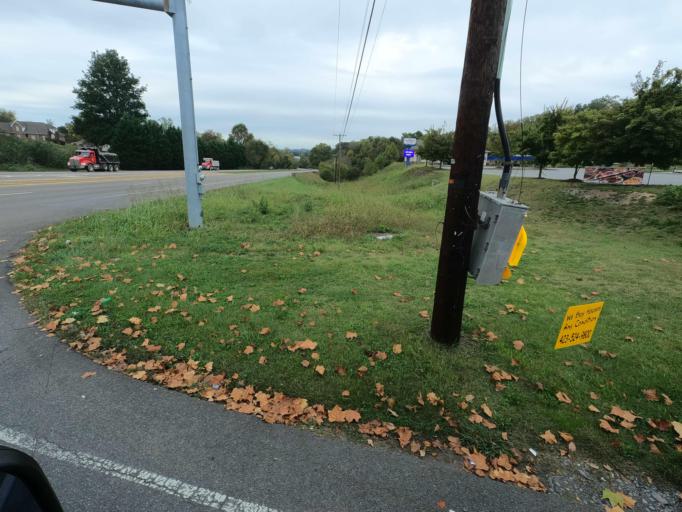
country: US
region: Tennessee
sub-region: Sullivan County
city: Kingsport
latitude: 36.5555
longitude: -82.6055
